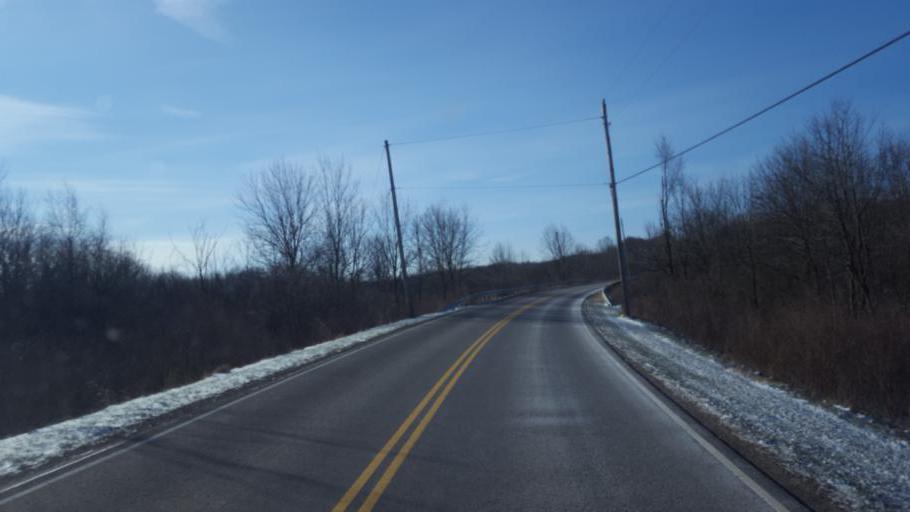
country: US
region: Ohio
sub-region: Knox County
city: Fredericktown
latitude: 40.5191
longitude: -82.5910
